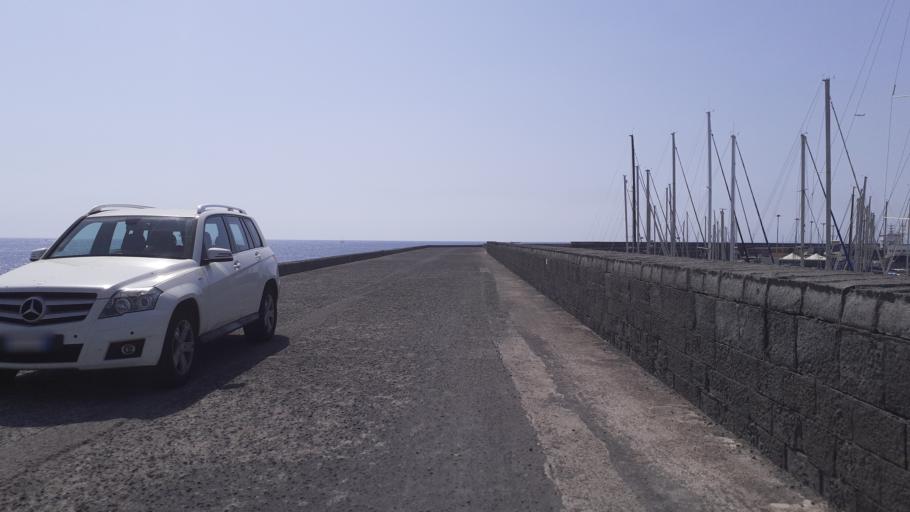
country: IT
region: Sicily
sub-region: Catania
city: Catania
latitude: 37.5013
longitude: 15.0981
